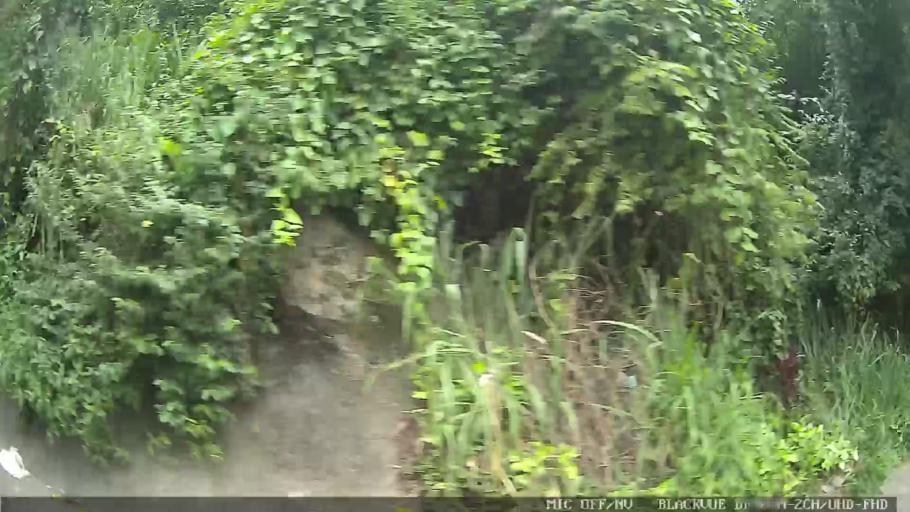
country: BR
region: Sao Paulo
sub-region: Guaruja
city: Guaruja
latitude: -23.9904
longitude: -46.2626
